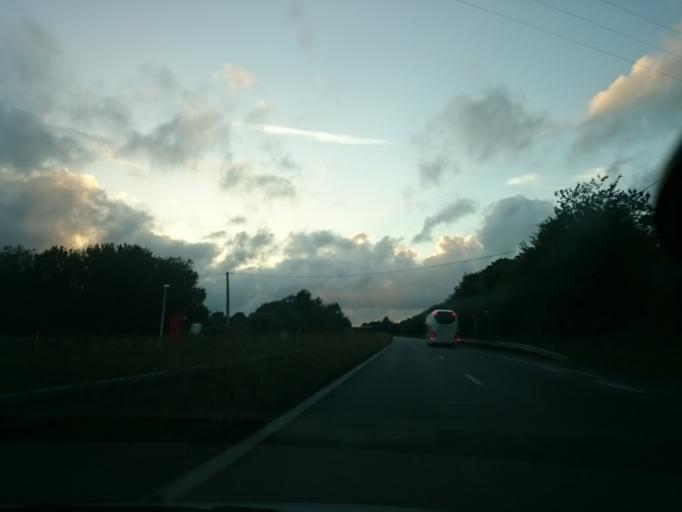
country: FR
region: Brittany
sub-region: Departement du Finistere
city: Redene
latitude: 47.8219
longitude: -3.4682
